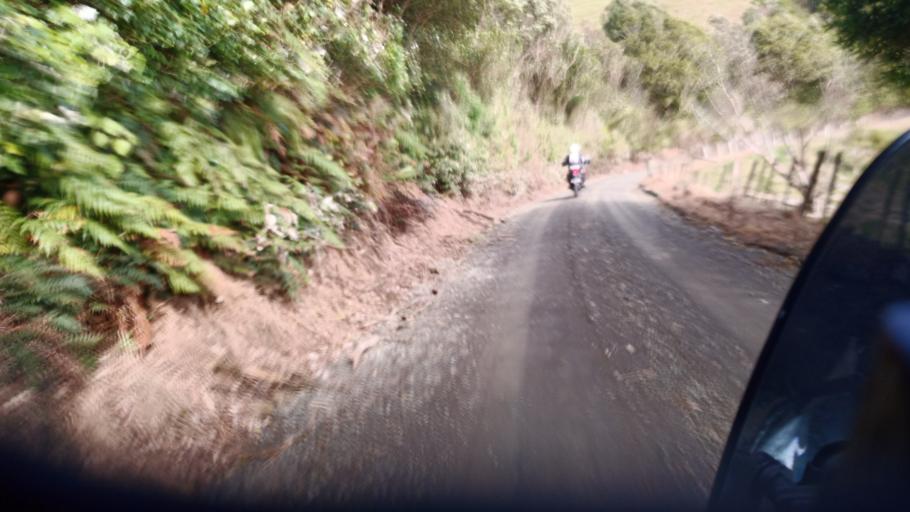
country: NZ
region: Gisborne
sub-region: Gisborne District
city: Gisborne
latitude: -38.4632
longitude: 177.5365
